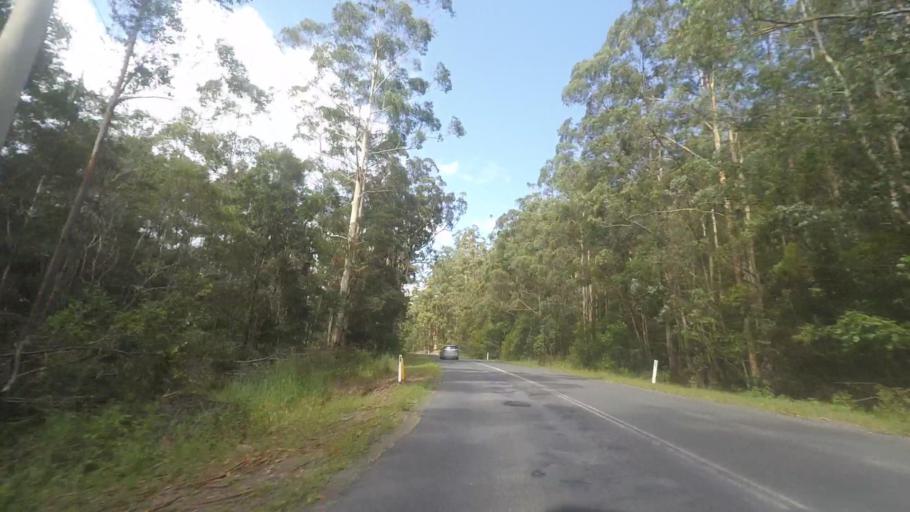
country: AU
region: New South Wales
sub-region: Great Lakes
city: Bulahdelah
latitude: -32.4006
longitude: 152.2888
